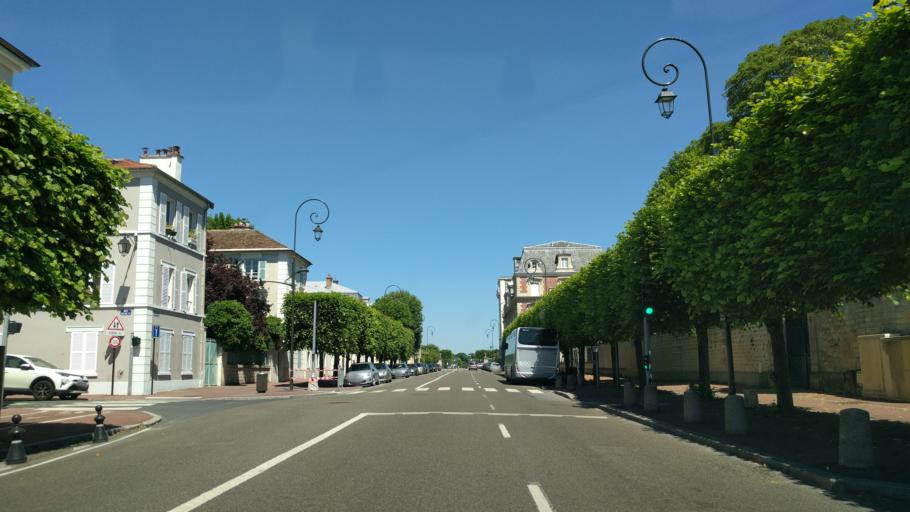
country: FR
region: Ile-de-France
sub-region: Departement des Yvelines
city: Le Pecq
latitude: 48.8962
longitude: 2.0985
